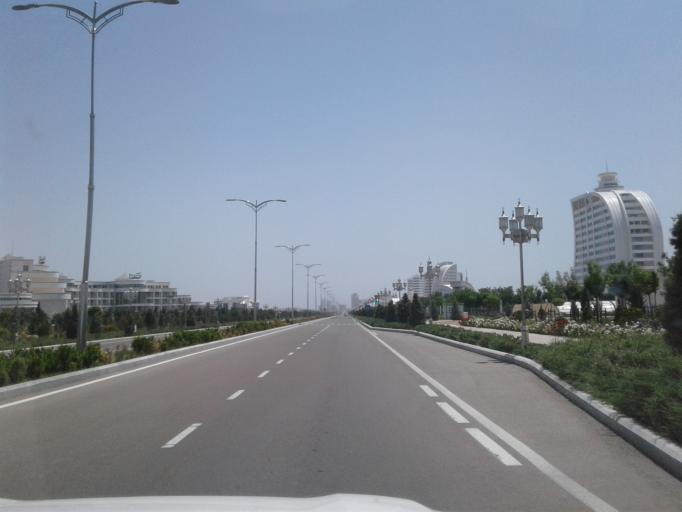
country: TM
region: Balkan
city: Turkmenbasy
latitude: 39.9831
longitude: 52.8264
